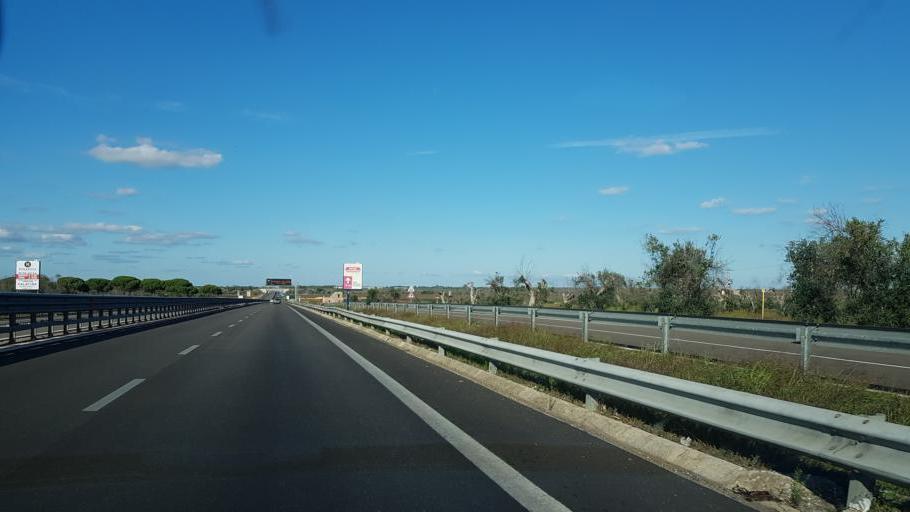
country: IT
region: Apulia
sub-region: Provincia di Lecce
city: Collemeto
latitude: 40.2461
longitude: 18.1136
